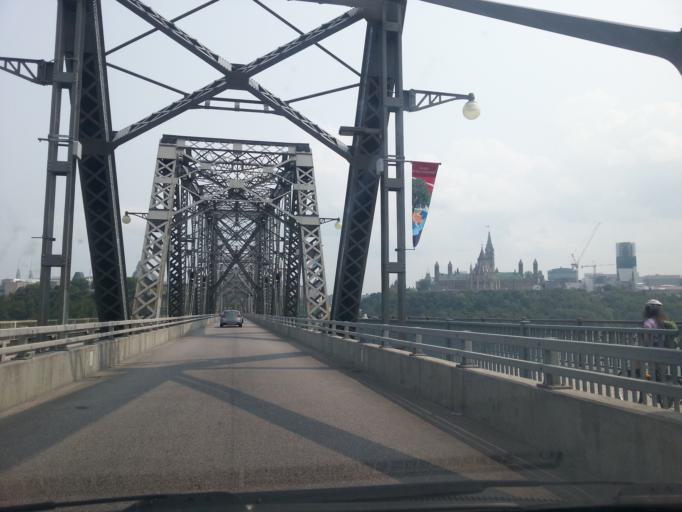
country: CA
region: Ontario
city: Ottawa
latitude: 45.4307
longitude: -75.7059
